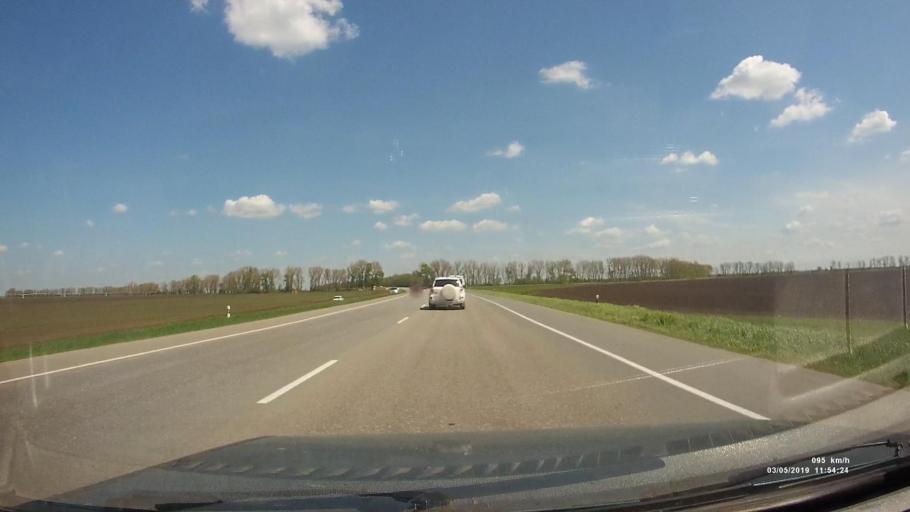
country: RU
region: Rostov
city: Bagayevskaya
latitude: 47.1698
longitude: 40.2795
